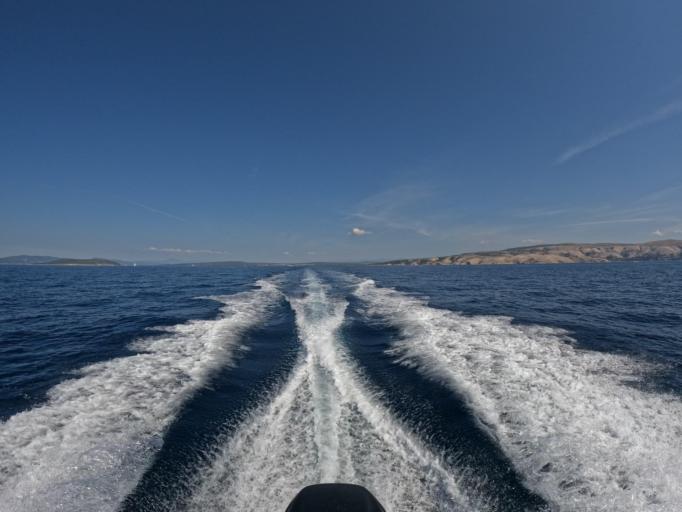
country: HR
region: Primorsko-Goranska
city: Punat
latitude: 44.9246
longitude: 14.6202
